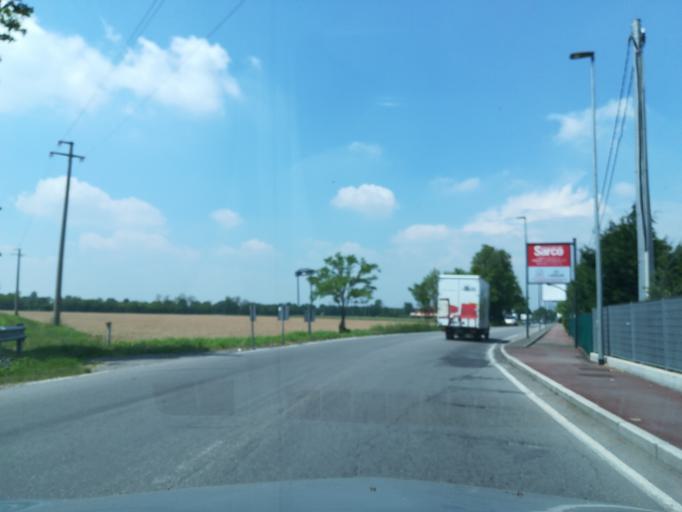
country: IT
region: Lombardy
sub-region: Provincia di Bergamo
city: Cavernago
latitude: 45.6328
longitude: 9.7626
